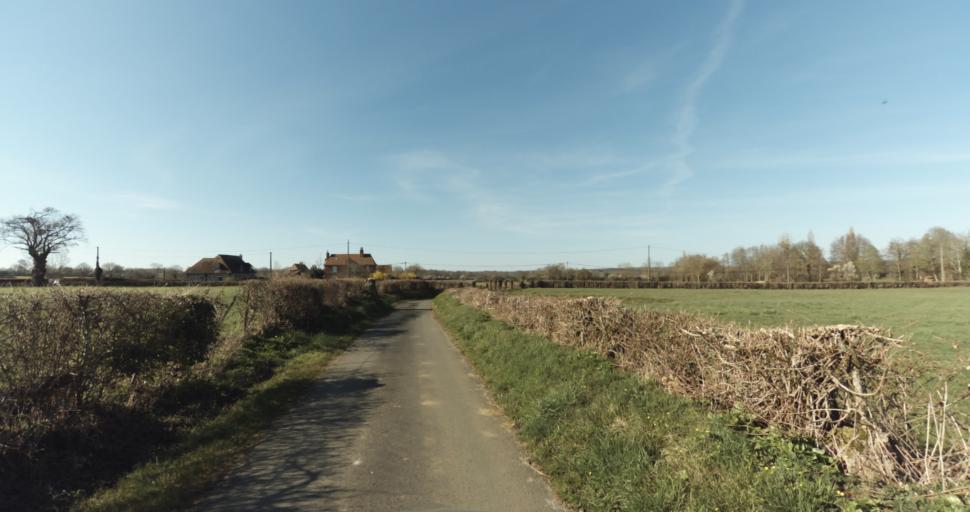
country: FR
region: Lower Normandy
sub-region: Departement du Calvados
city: Saint-Pierre-sur-Dives
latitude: 49.0406
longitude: 0.0572
